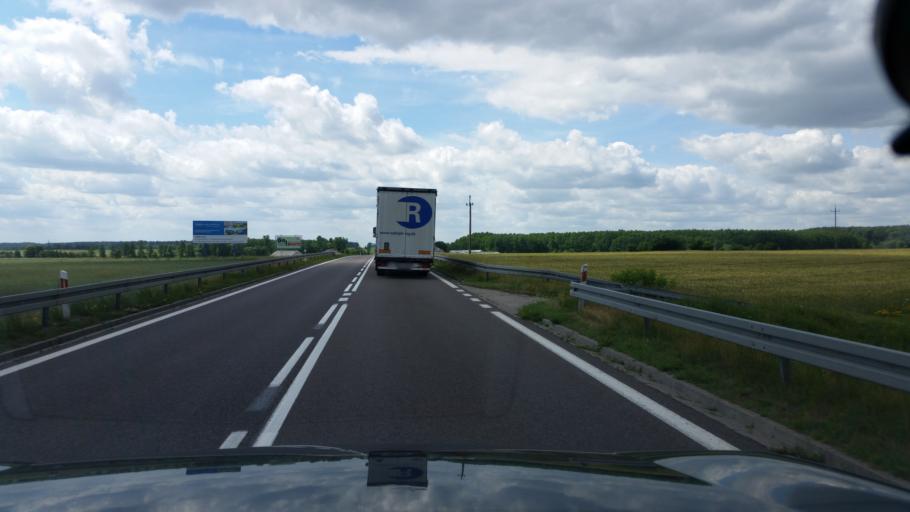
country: PL
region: Podlasie
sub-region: Powiat grajewski
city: Szczuczyn
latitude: 53.4953
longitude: 22.2277
